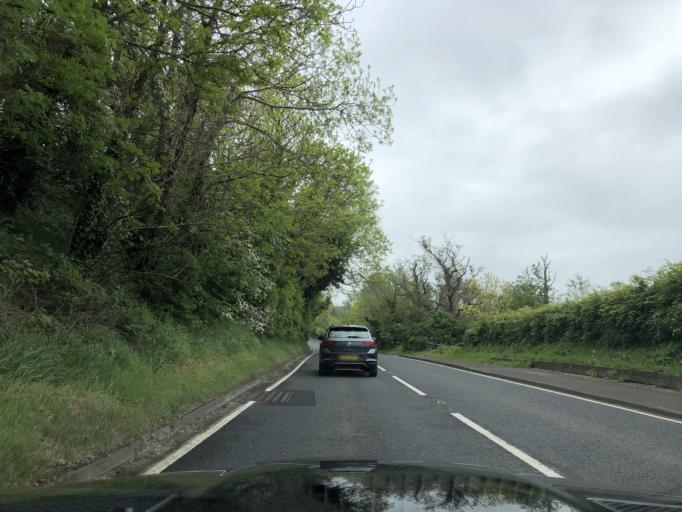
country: GB
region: Northern Ireland
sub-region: Down District
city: Downpatrick
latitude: 54.3195
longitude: -5.7245
